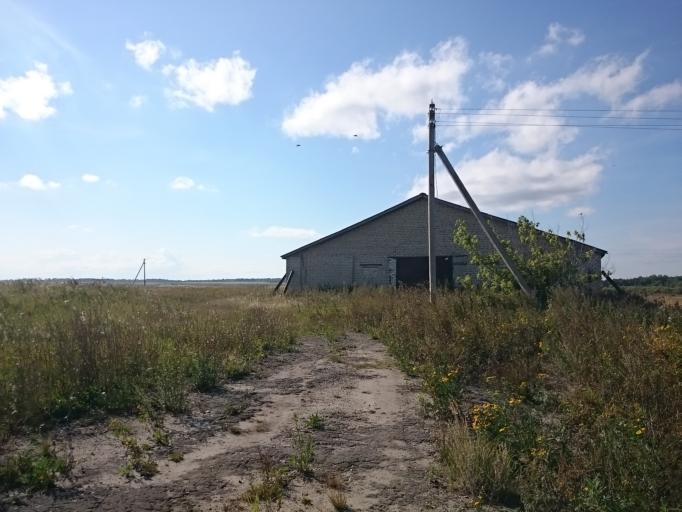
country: RU
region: Mordoviya
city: Kadoshkino
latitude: 54.0319
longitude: 44.4888
